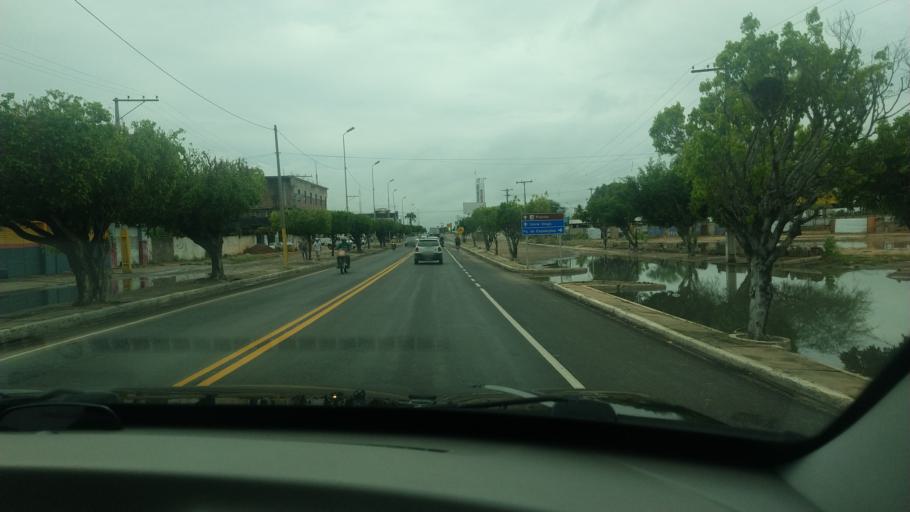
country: BR
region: Bahia
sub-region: Paulo Afonso
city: Paulo Afonso
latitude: -9.4066
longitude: -38.2372
